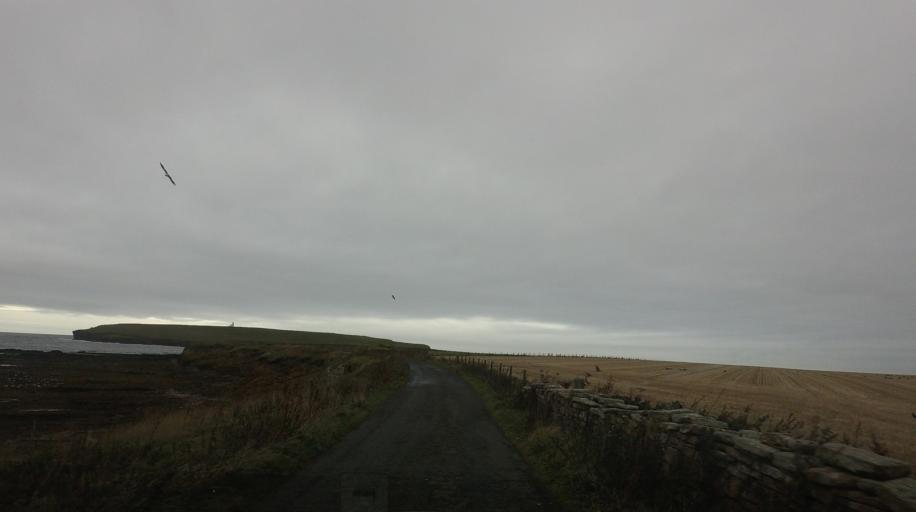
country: GB
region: Scotland
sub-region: Orkney Islands
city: Stromness
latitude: 59.1330
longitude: -3.3183
